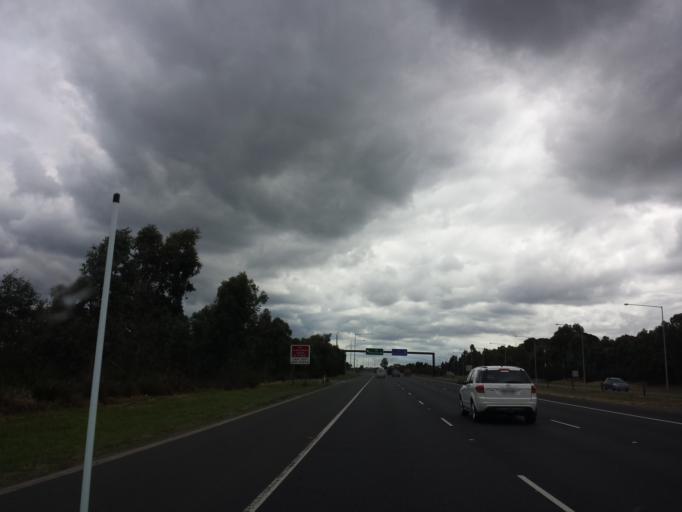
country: AU
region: Victoria
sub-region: Knox
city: Wantirna
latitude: -37.8528
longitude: 145.2147
